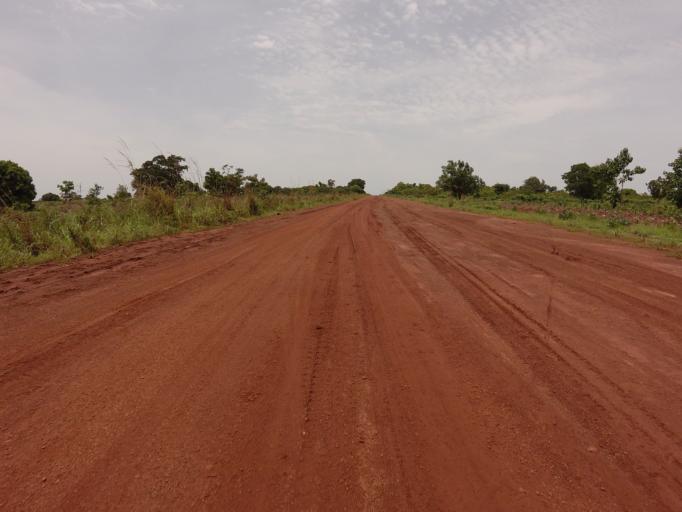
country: GH
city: Kpandae
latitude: 8.7605
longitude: 0.0608
